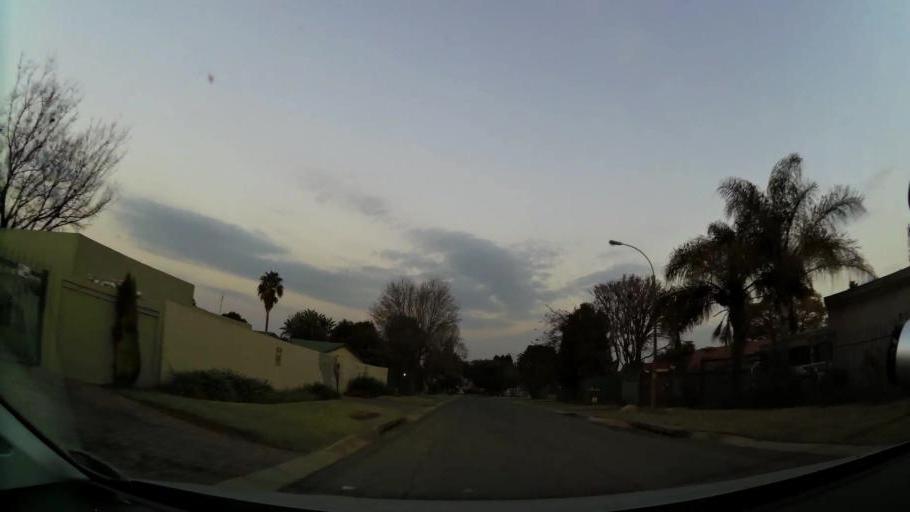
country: ZA
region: Gauteng
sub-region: Ekurhuleni Metropolitan Municipality
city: Tembisa
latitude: -26.0521
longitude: 28.2448
